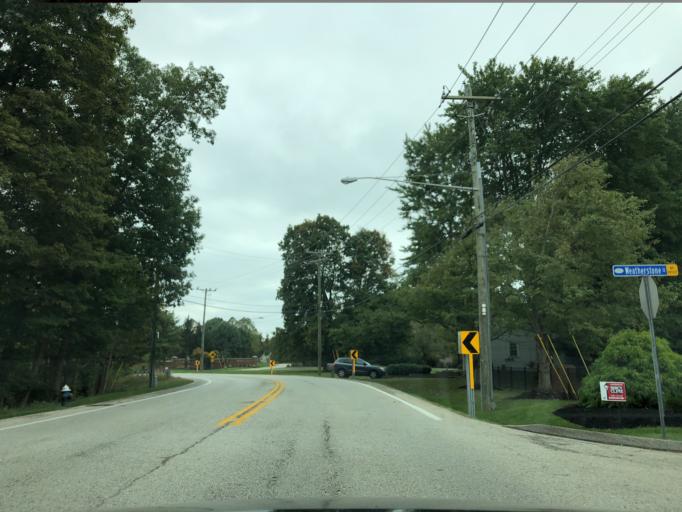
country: US
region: Ohio
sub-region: Hamilton County
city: The Village of Indian Hill
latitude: 39.2604
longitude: -84.3078
